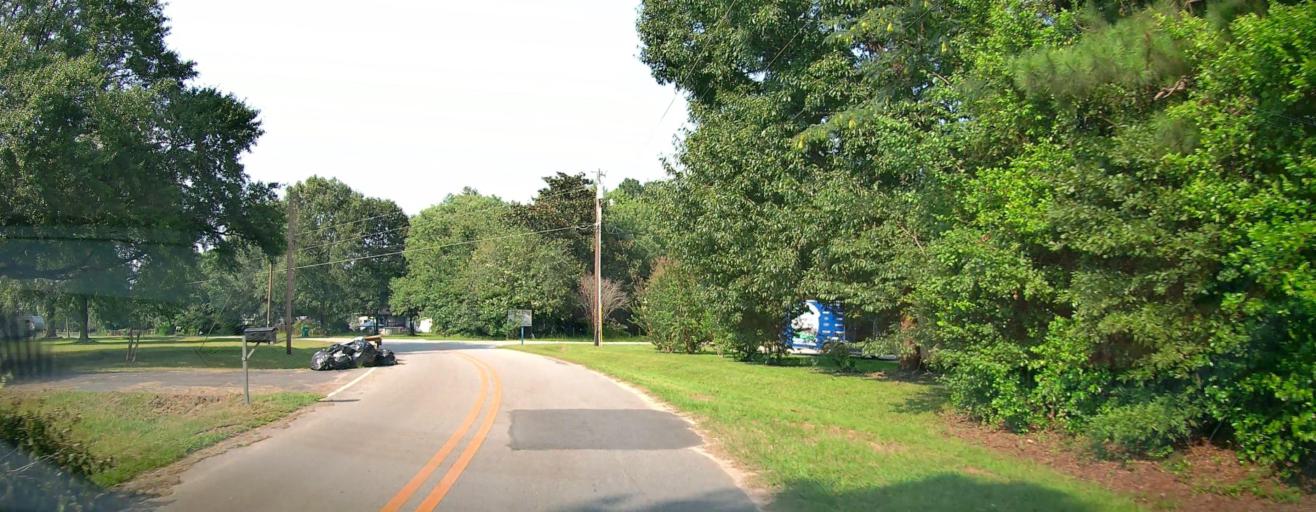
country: US
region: Georgia
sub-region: Houston County
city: Centerville
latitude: 32.6475
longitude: -83.6921
